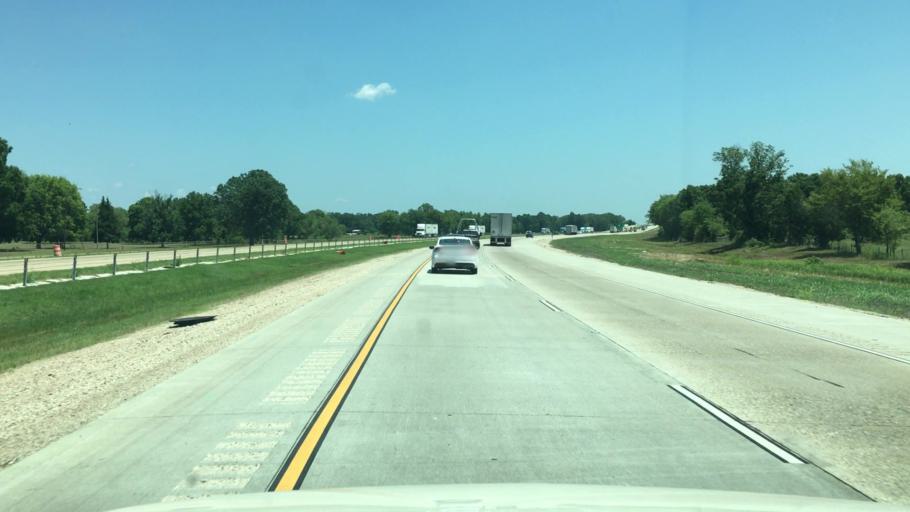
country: US
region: Arkansas
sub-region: Miller County
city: Texarkana
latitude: 33.5472
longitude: -93.8859
